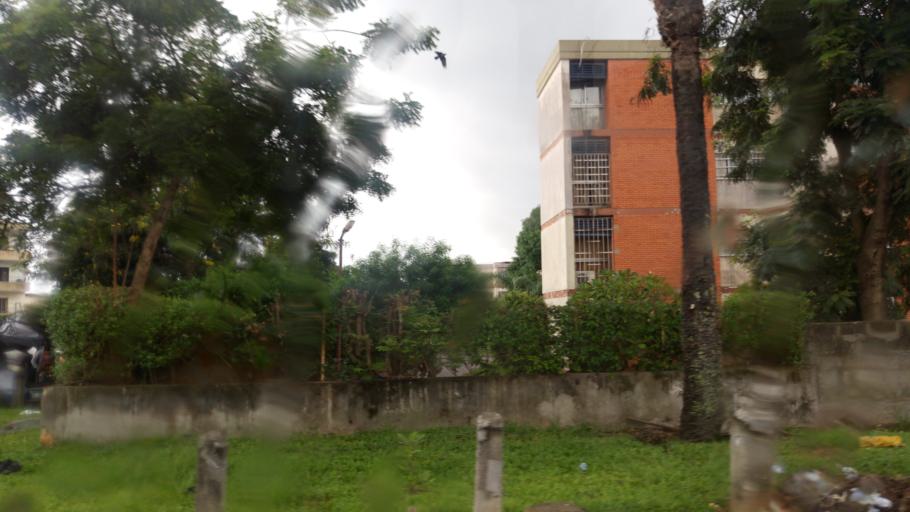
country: CI
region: Lagunes
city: Abobo
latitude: 5.3661
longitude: -3.9897
